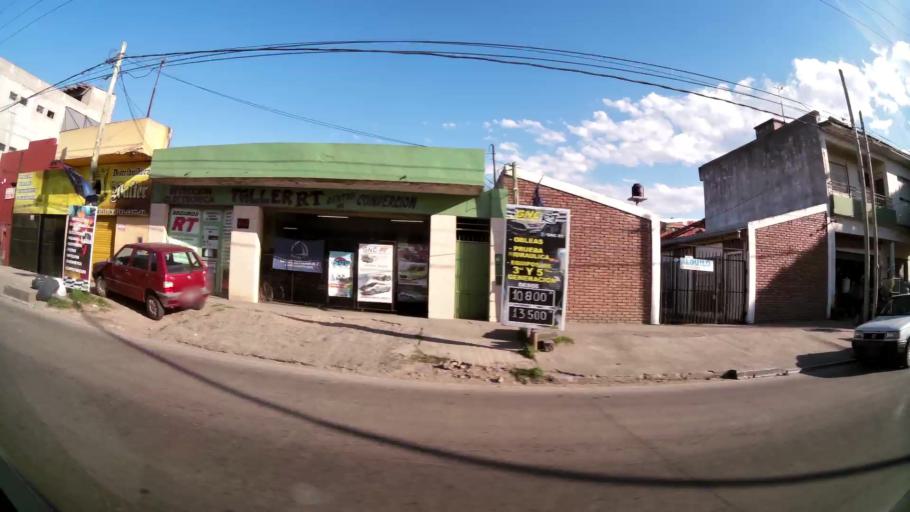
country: AR
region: Buenos Aires
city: Hurlingham
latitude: -34.5060
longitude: -58.7211
